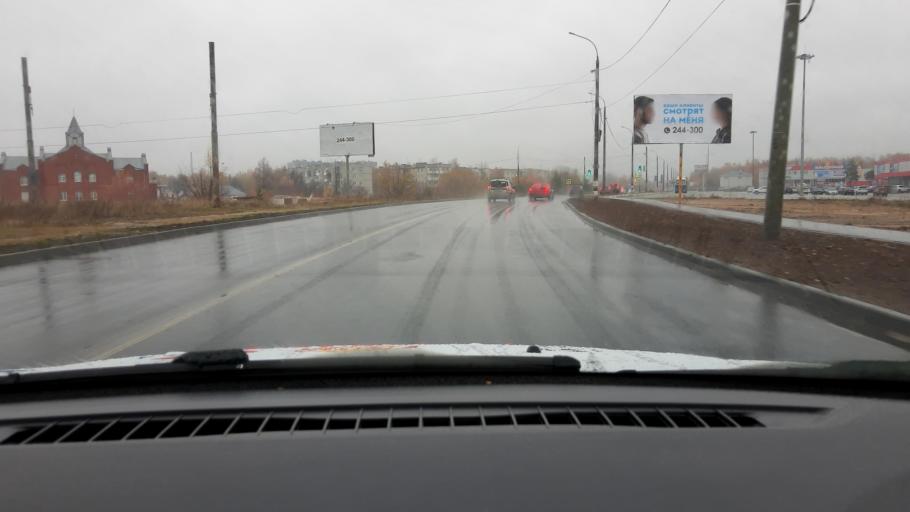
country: RU
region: Nizjnij Novgorod
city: Dzerzhinsk
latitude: 56.2397
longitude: 43.4070
